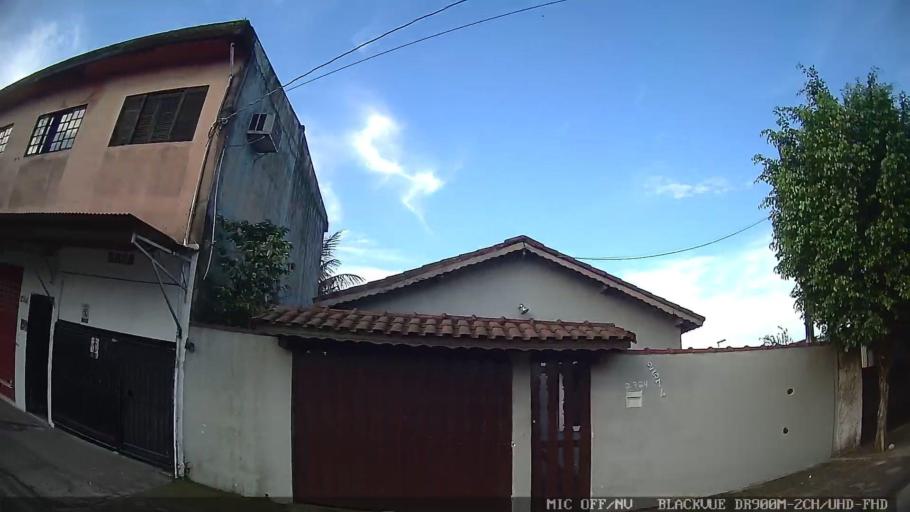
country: BR
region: Sao Paulo
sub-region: Itanhaem
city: Itanhaem
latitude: -24.1574
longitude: -46.7830
